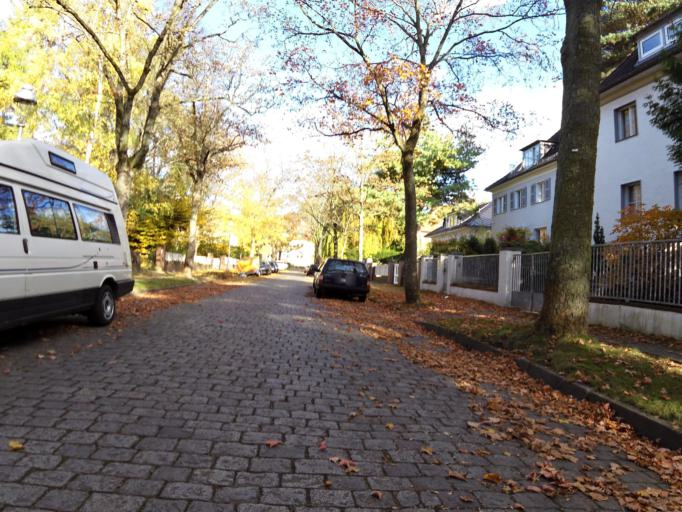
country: DE
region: Berlin
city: Zehlendorf Bezirk
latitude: 52.4442
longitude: 13.2337
